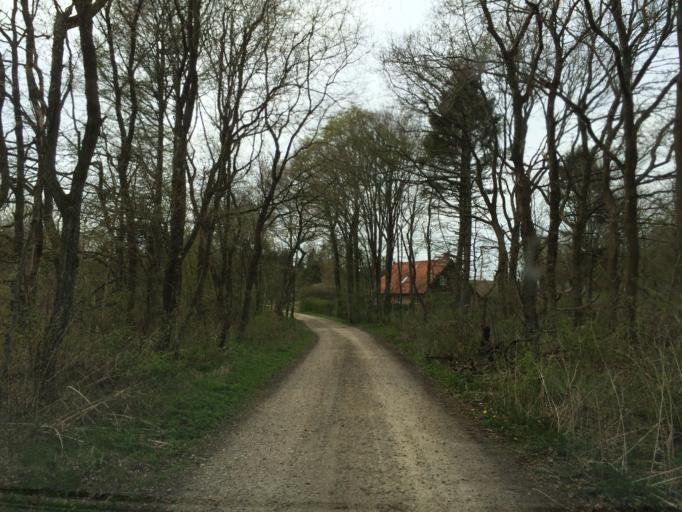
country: DK
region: Central Jutland
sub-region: Holstebro Kommune
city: Ulfborg
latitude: 56.2223
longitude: 8.4730
